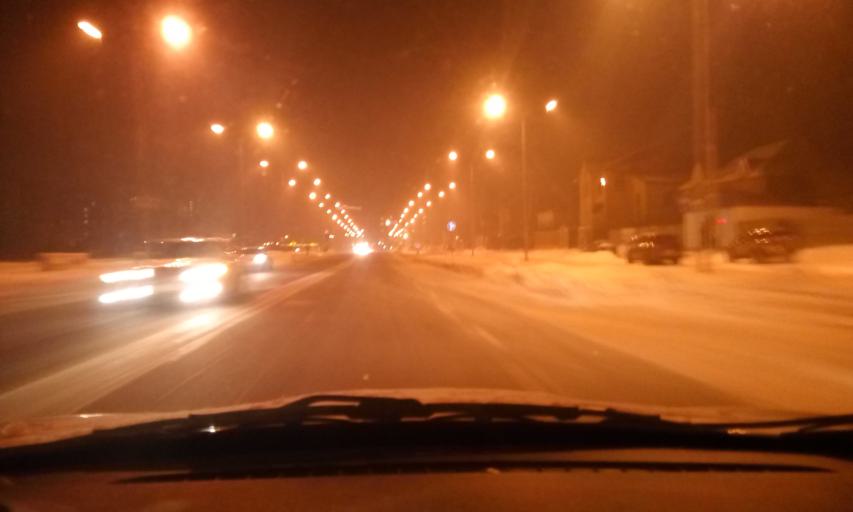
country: KZ
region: Astana Qalasy
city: Astana
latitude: 51.1306
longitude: 71.4921
